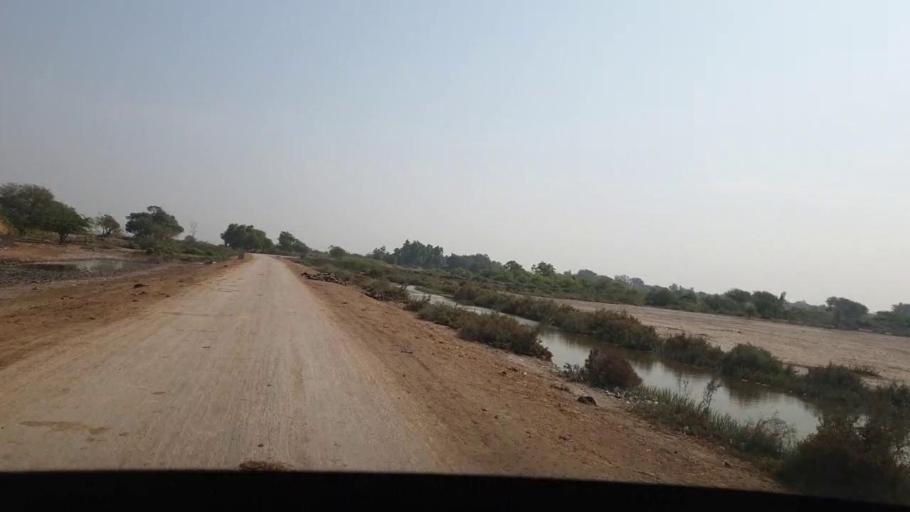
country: PK
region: Sindh
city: Chuhar Jamali
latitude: 24.2688
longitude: 67.9397
